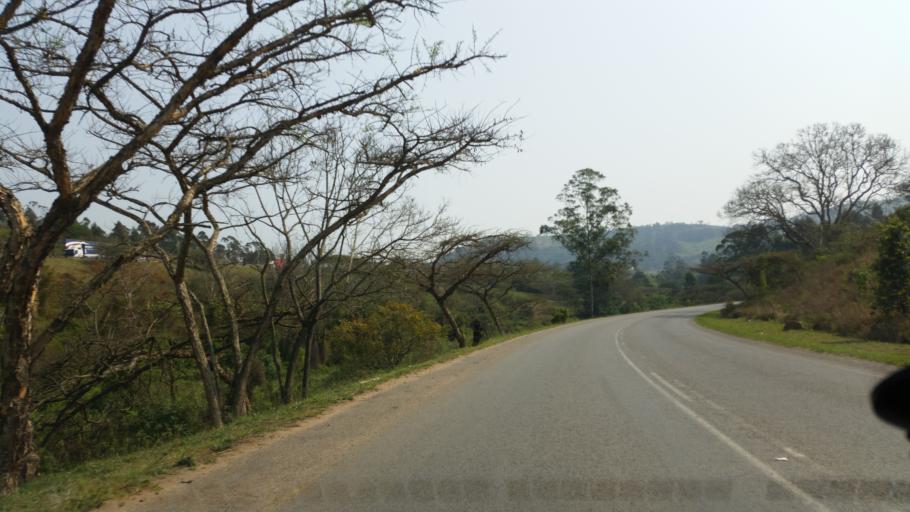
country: ZA
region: KwaZulu-Natal
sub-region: eThekwini Metropolitan Municipality
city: Mpumalanga
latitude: -29.7677
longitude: 30.6829
